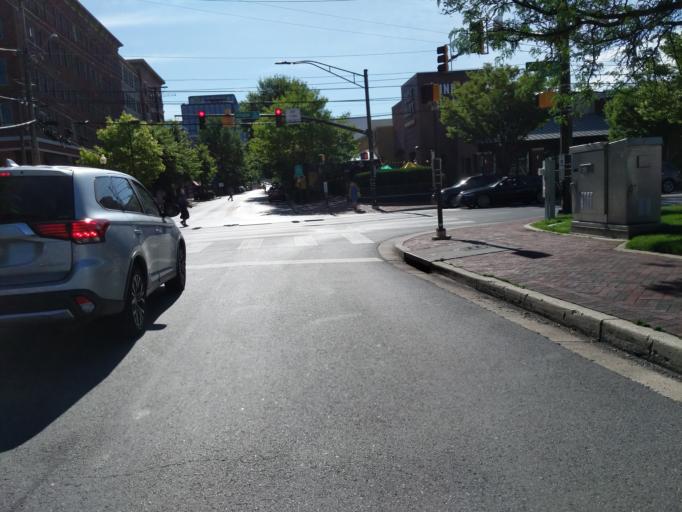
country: US
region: Maryland
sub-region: Montgomery County
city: Bethesda
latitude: 38.9808
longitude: -77.0987
